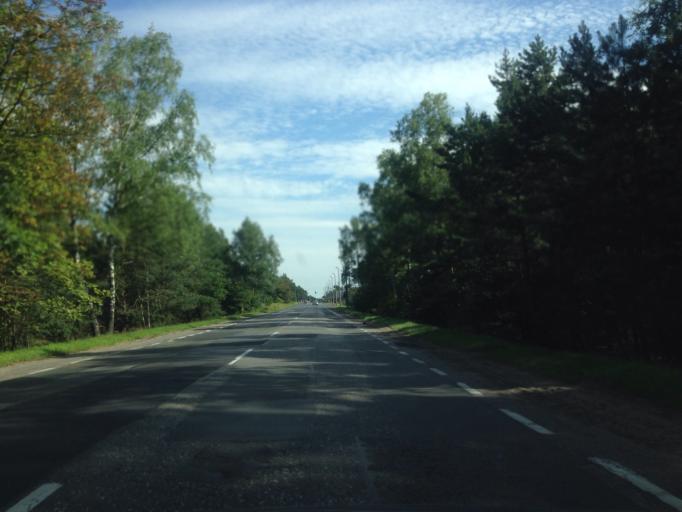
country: PL
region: Kujawsko-Pomorskie
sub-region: Torun
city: Torun
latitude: 52.9791
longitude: 18.6733
